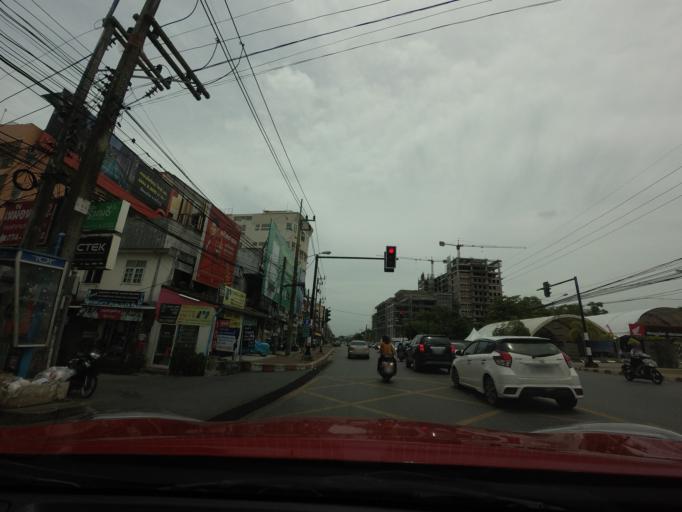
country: TH
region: Songkhla
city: Hat Yai
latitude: 7.0018
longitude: 100.5005
